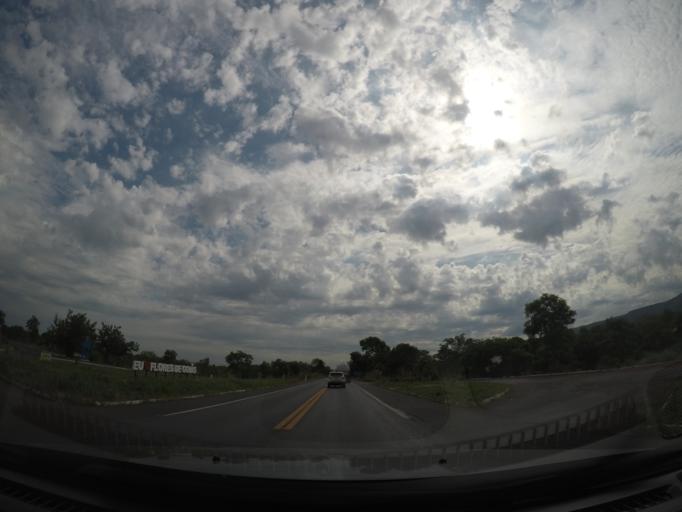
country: BR
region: Goias
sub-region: Formosa
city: Formosa
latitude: -14.9186
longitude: -46.9590
